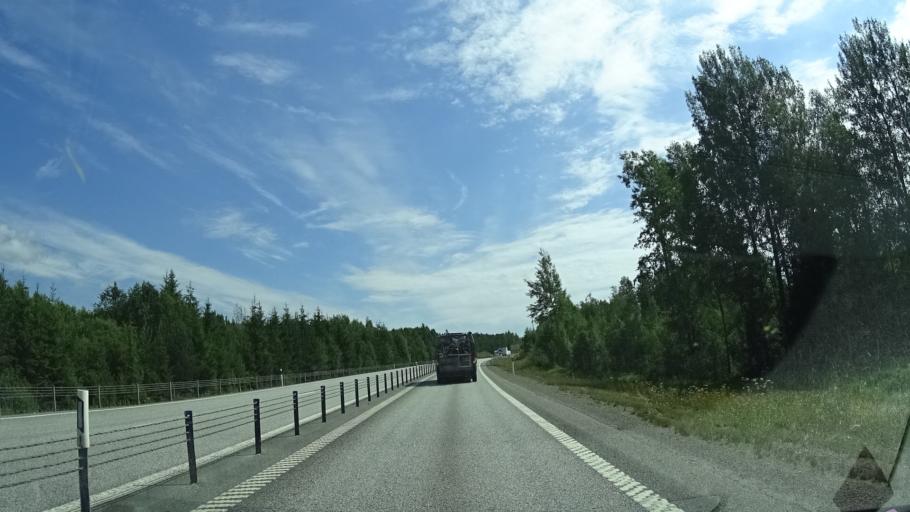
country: SE
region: OErebro
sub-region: Karlskoga Kommun
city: Karlskoga
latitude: 59.3267
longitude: 14.4365
